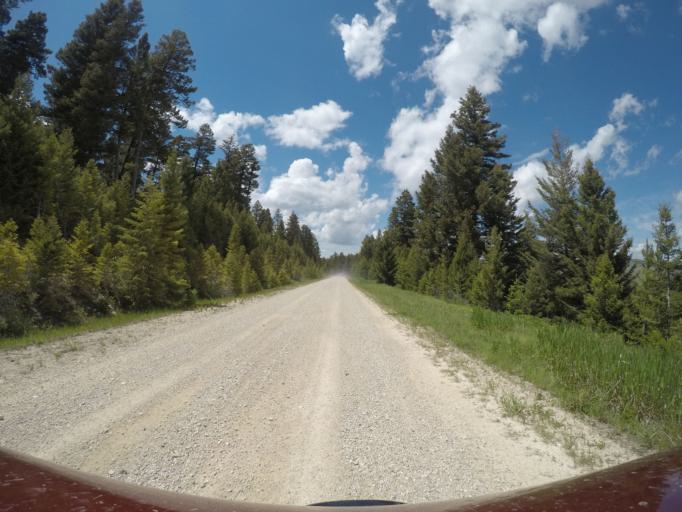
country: US
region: Wyoming
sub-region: Big Horn County
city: Lovell
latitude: 45.1985
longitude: -108.4984
